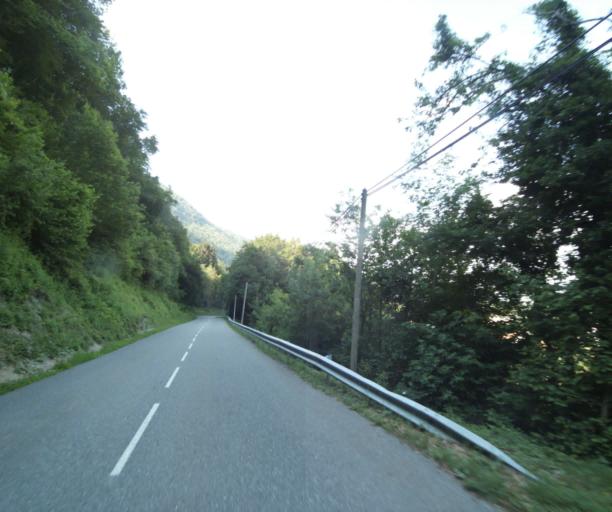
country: FR
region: Rhone-Alpes
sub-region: Departement de la Haute-Savoie
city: Lyaud
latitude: 46.3143
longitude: 6.4987
